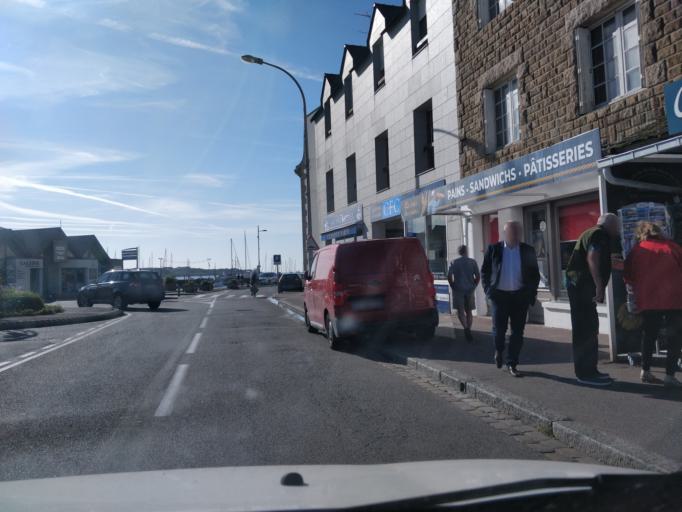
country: FR
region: Brittany
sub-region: Departement du Morbihan
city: La Trinite-sur-Mer
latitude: 47.5874
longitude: -3.0277
